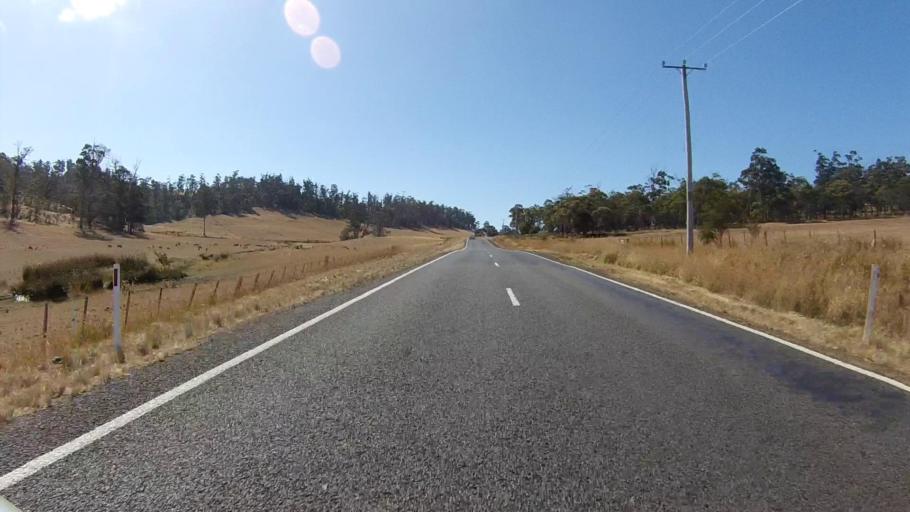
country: AU
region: Tasmania
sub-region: Sorell
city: Sorell
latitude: -42.4322
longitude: 147.9313
